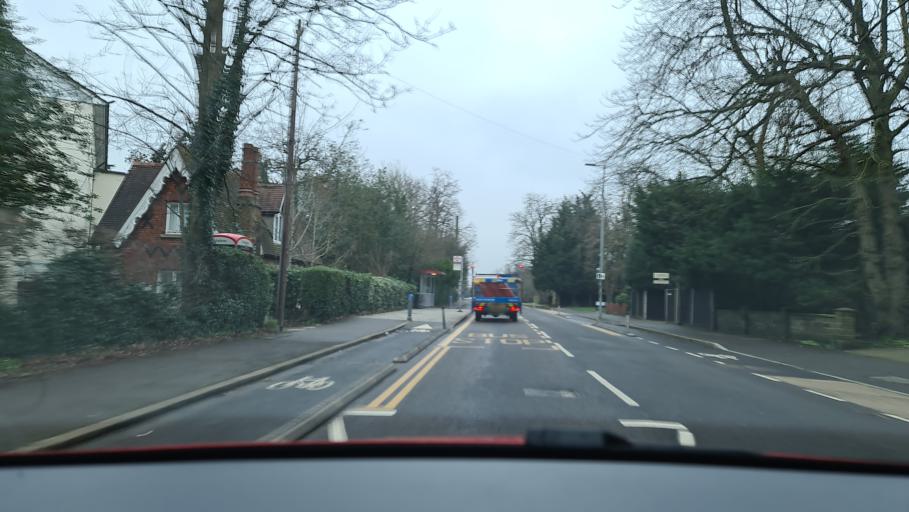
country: GB
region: England
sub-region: Greater London
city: Kingston upon Thames
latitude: 51.4218
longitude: -0.2771
